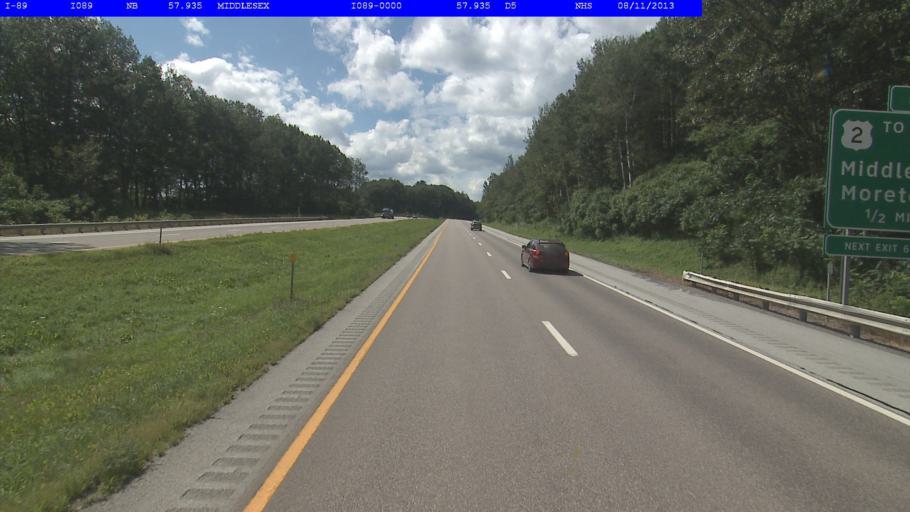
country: US
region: Vermont
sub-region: Washington County
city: Waterbury
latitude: 44.2924
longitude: -72.6720
